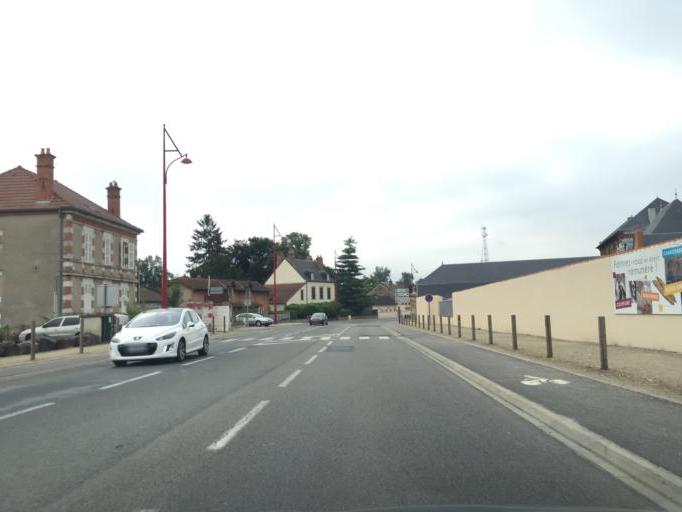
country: FR
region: Auvergne
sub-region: Departement de l'Allier
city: Moulins
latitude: 46.5799
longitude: 3.3225
